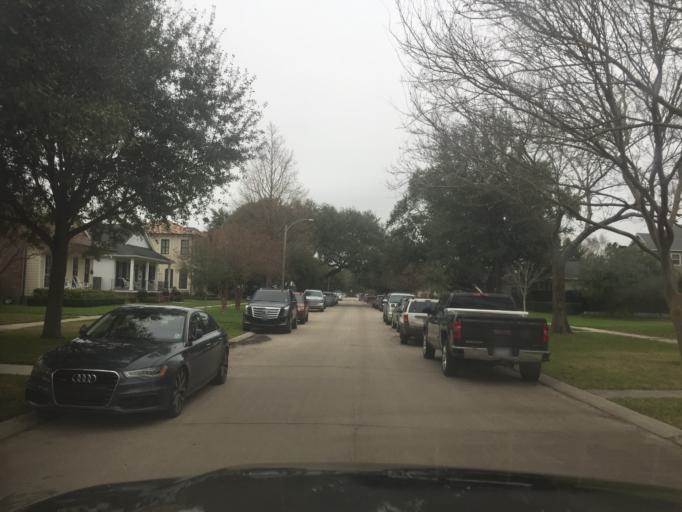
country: US
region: Louisiana
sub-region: Jefferson Parish
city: Metairie
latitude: 29.9970
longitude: -90.1036
